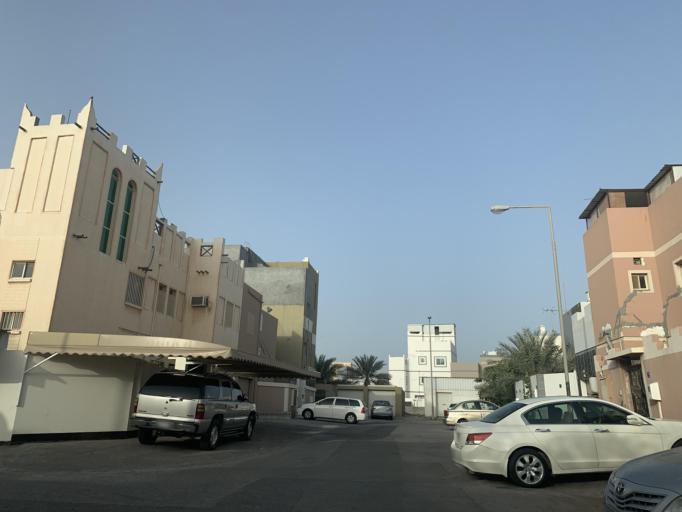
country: BH
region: Northern
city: Madinat `Isa
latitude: 26.1609
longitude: 50.5108
